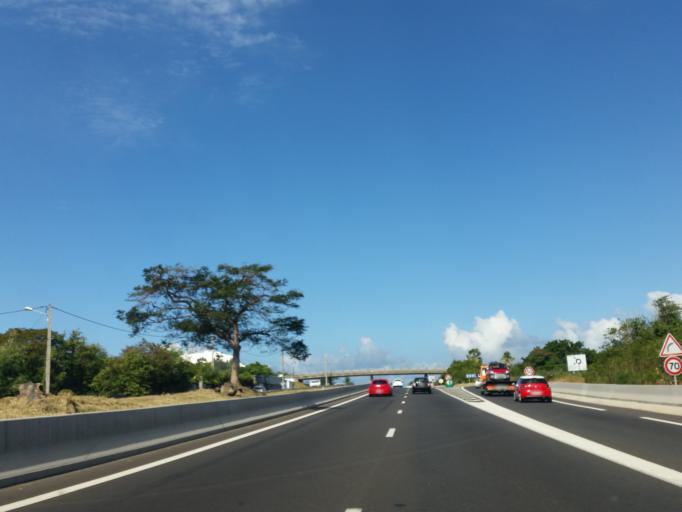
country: RE
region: Reunion
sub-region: Reunion
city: Saint-Louis
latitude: -21.3034
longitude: 55.4269
